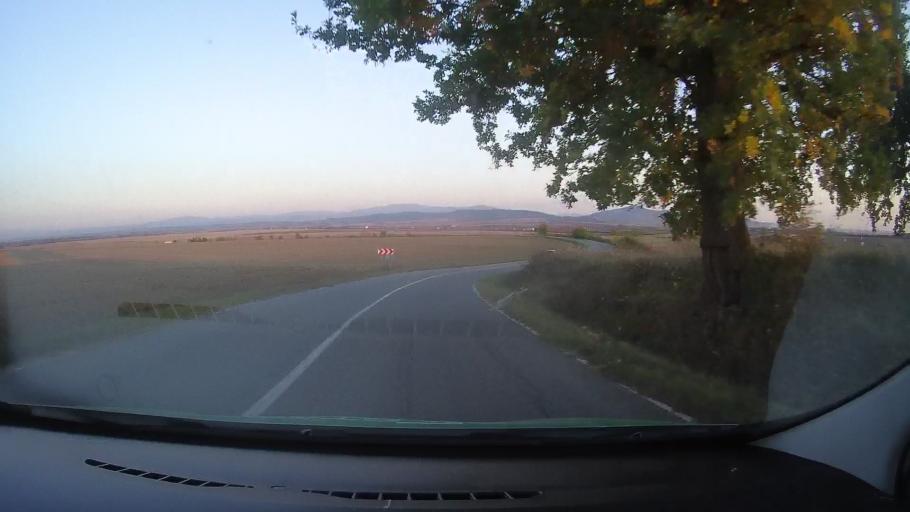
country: RO
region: Timis
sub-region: Comuna Manastiur
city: Manastiur
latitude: 45.8179
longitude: 22.0717
